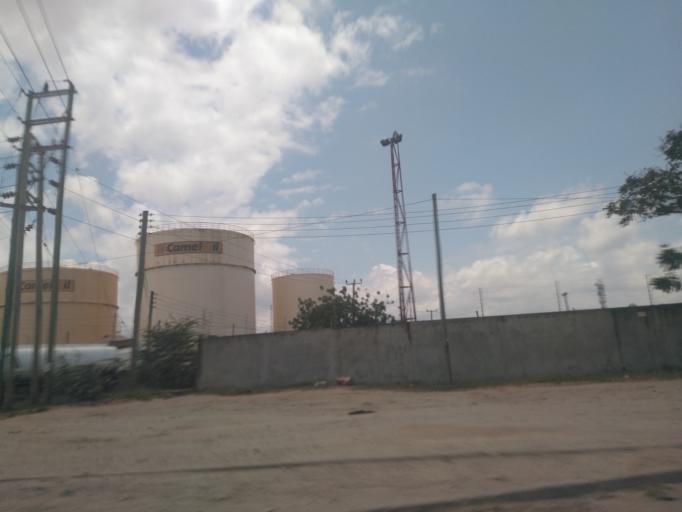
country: TZ
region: Dar es Salaam
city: Dar es Salaam
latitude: -6.8400
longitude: 39.2923
